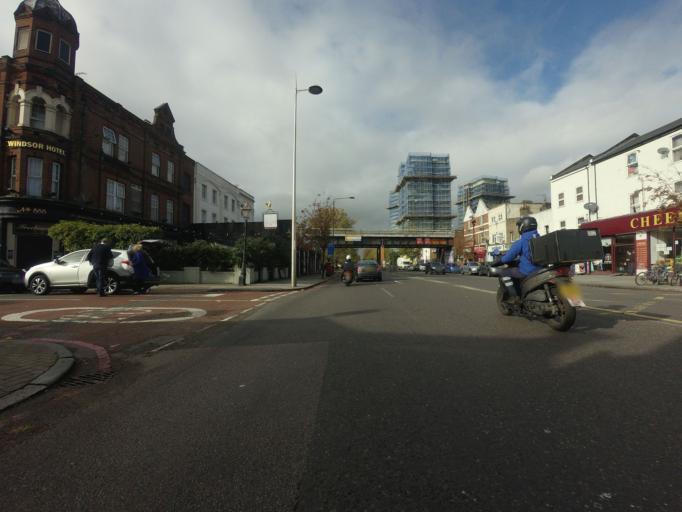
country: GB
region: England
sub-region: Greater London
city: Camberwell
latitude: 51.4783
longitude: -0.0535
